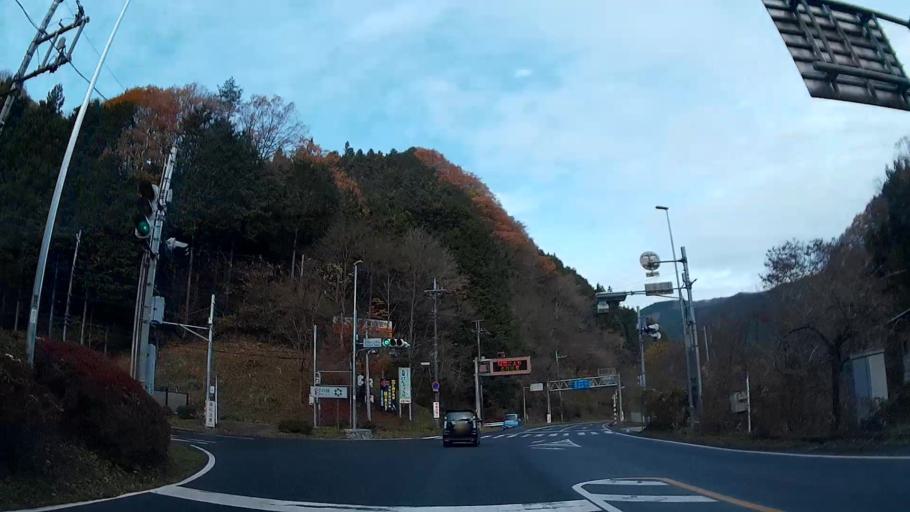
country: JP
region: Saitama
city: Chichibu
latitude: 35.9619
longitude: 139.1616
